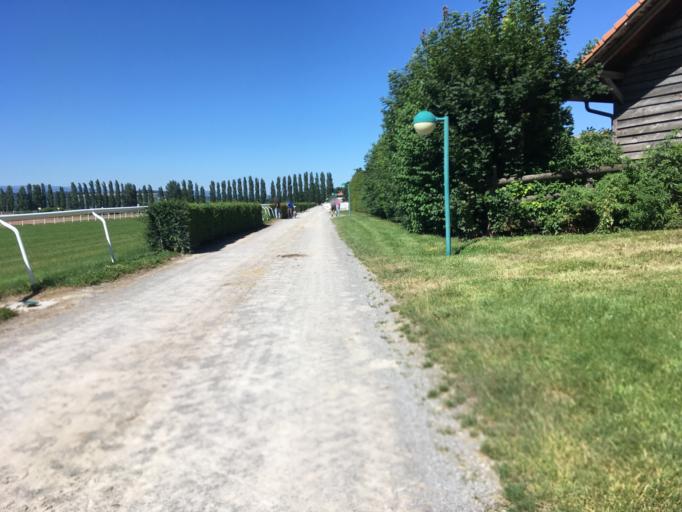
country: CH
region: Fribourg
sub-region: Broye District
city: Domdidier
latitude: 46.8832
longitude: 7.0093
